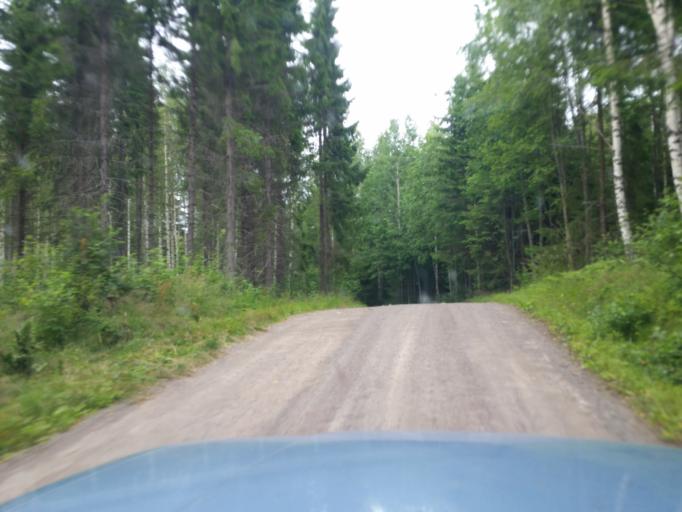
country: FI
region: Uusimaa
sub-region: Helsinki
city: Kaerkoelae
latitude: 60.5680
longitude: 24.0040
